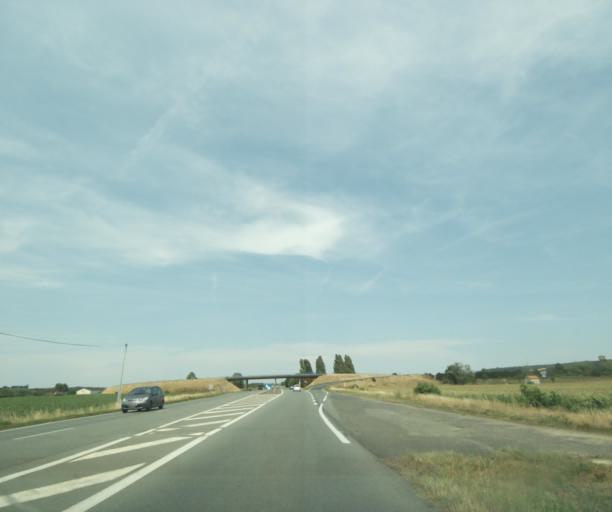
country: FR
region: Poitou-Charentes
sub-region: Departement de la Vienne
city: Dange-Saint-Romain
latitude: 46.8965
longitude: 0.5710
